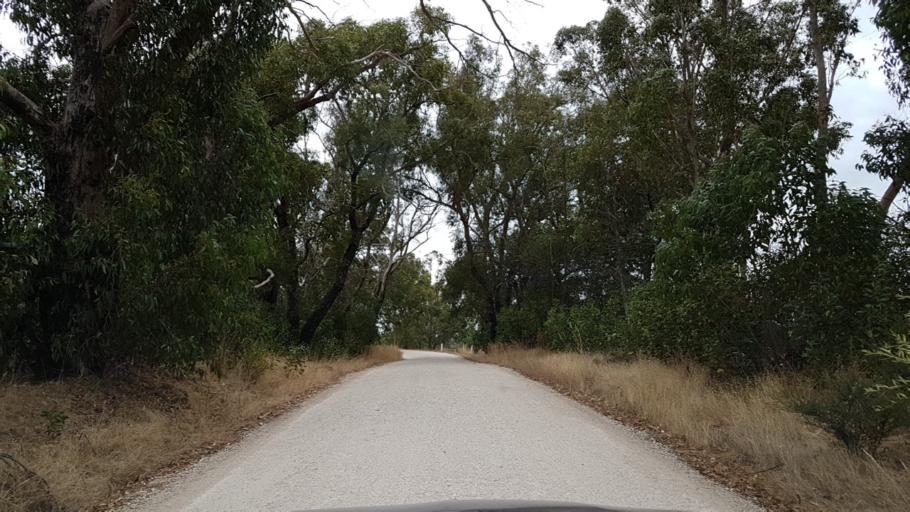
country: AU
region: South Australia
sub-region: Adelaide Hills
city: Gumeracha
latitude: -34.7989
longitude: 138.8173
